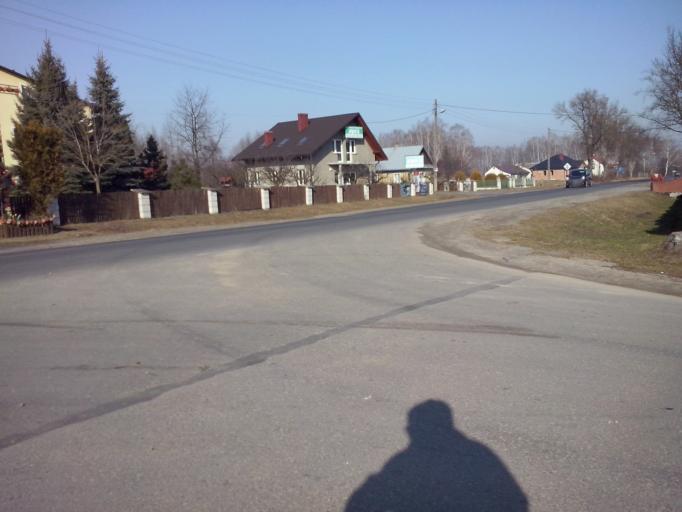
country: PL
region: Subcarpathian Voivodeship
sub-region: Powiat nizanski
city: Krzeszow
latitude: 50.4162
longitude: 22.3499
